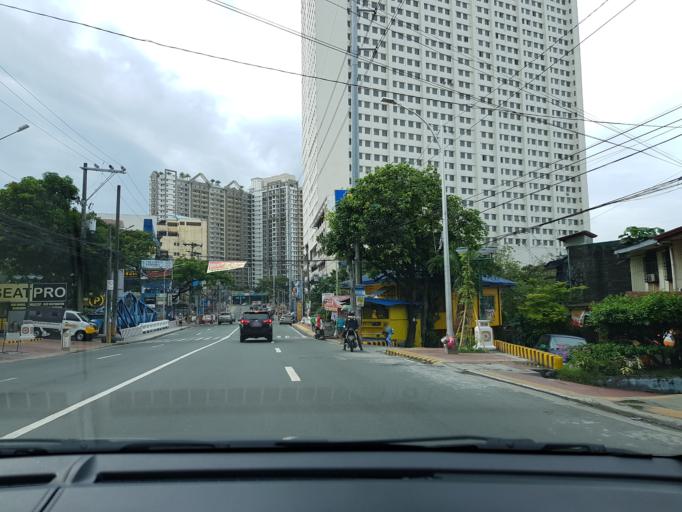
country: PH
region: Calabarzon
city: Del Monte
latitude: 14.6266
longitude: 121.0335
